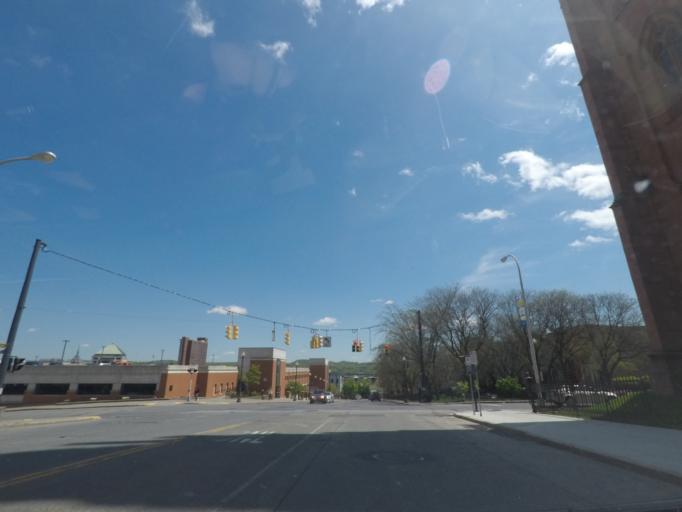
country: US
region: New York
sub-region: Albany County
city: Albany
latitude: 42.6477
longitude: -73.7595
